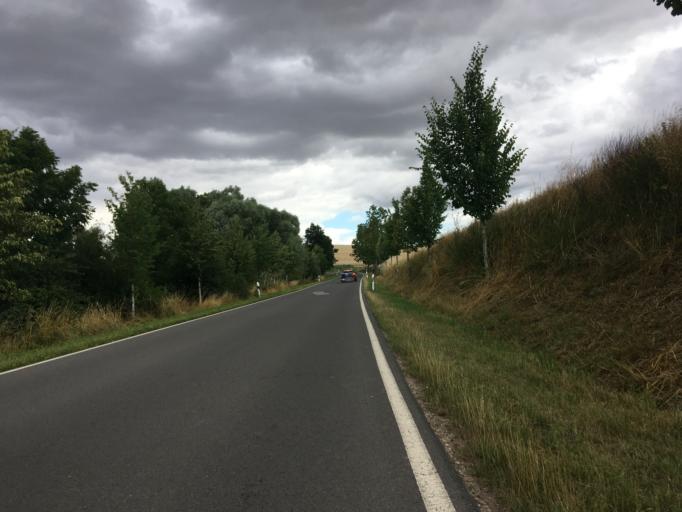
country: DE
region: Brandenburg
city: Gramzow
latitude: 53.2312
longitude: 13.9438
